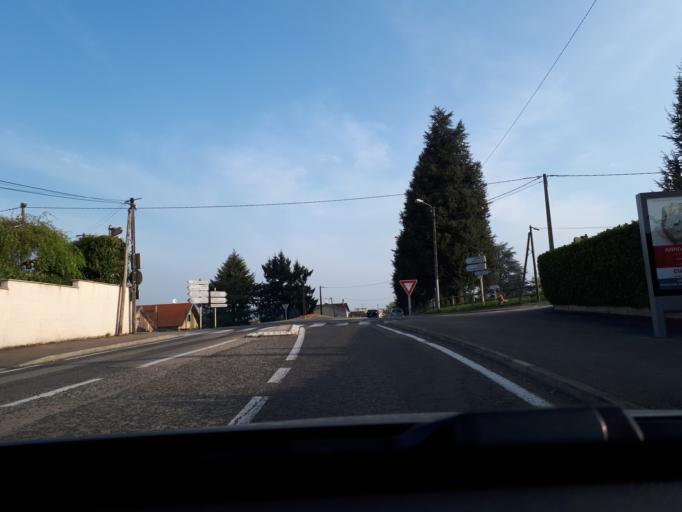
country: FR
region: Rhone-Alpes
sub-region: Departement de l'Isere
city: Bourgoin-Jallieu
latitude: 45.6064
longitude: 5.2723
